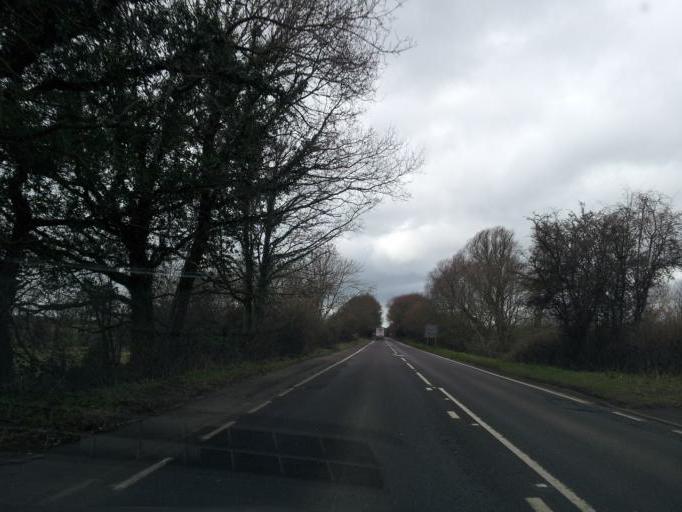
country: GB
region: England
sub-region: Somerset
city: Stoke-sub-Hamdon
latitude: 50.9599
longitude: -2.7232
